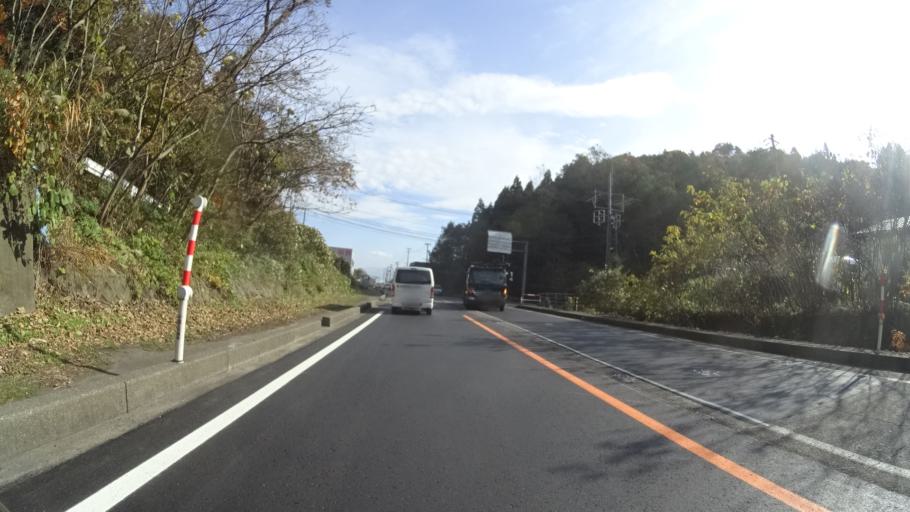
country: JP
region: Niigata
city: Joetsu
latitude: 37.1630
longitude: 138.2154
